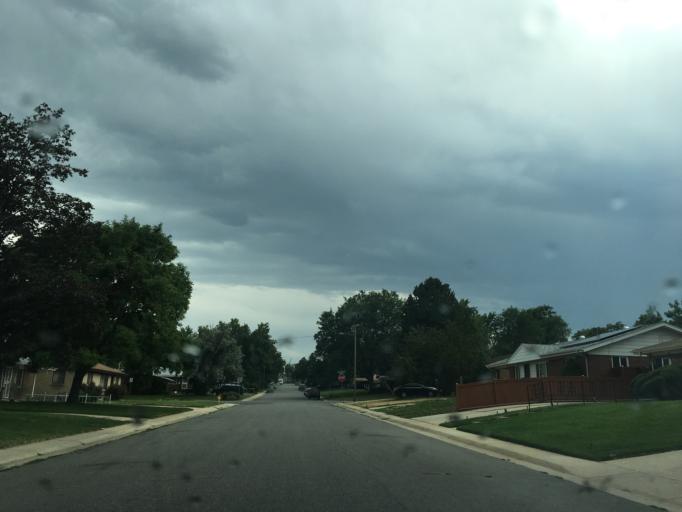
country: US
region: Colorado
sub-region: Arapahoe County
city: Sheridan
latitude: 39.6711
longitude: -105.0397
